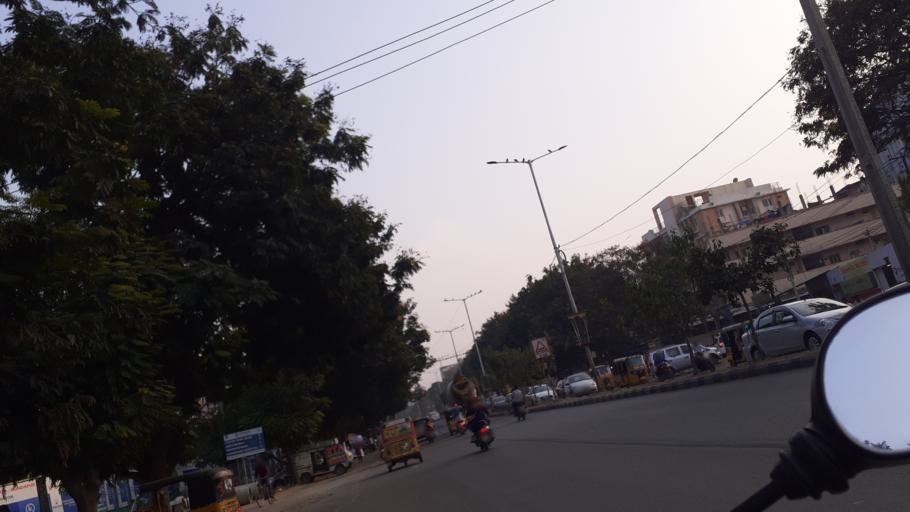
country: IN
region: Telangana
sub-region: Rangareddi
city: Kukatpalli
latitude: 17.4726
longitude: 78.3646
